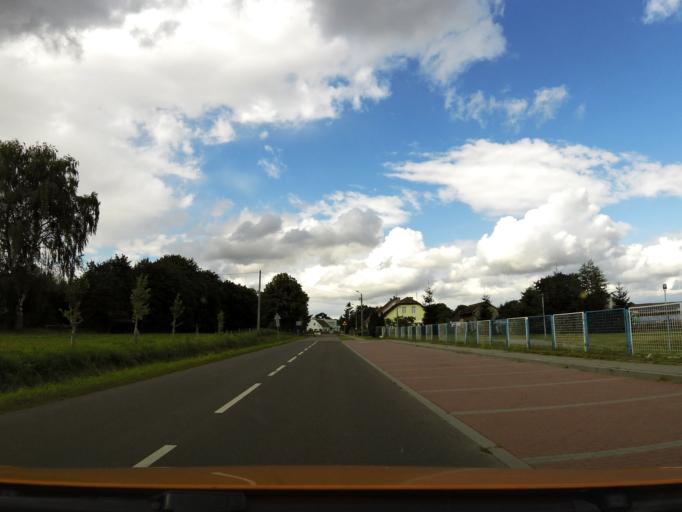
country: PL
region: West Pomeranian Voivodeship
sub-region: Powiat kolobrzeski
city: Ryman
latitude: 53.9918
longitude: 15.4916
